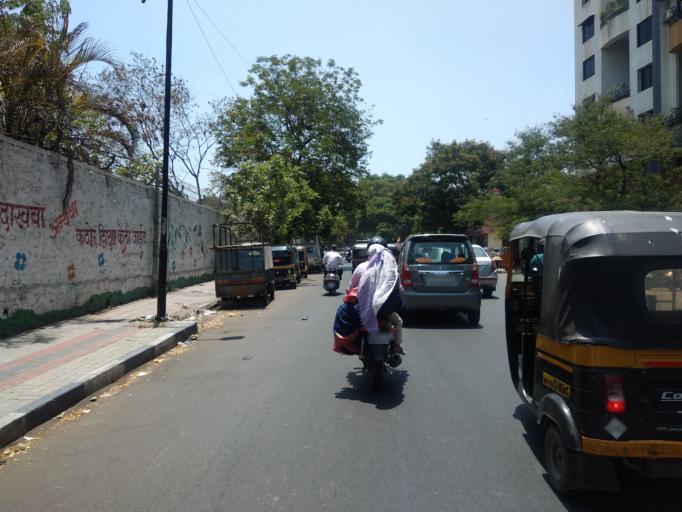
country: IN
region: Maharashtra
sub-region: Pune Division
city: Pune
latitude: 18.5041
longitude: 73.8477
